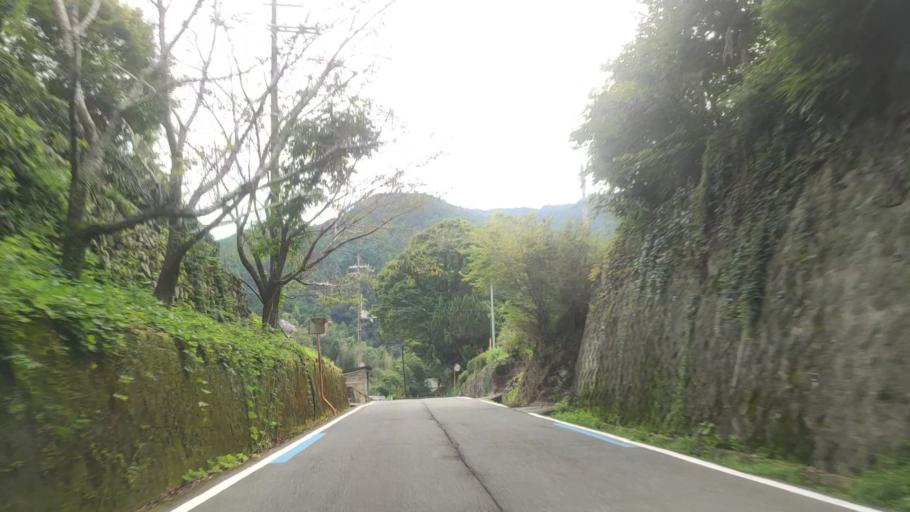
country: JP
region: Wakayama
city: Koya
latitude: 34.2575
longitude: 135.5444
